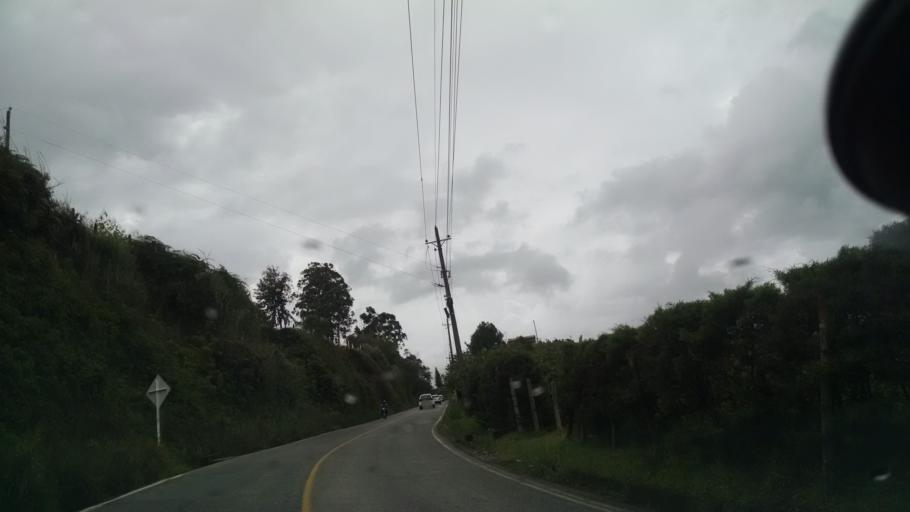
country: CO
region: Antioquia
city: Guatape
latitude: 6.2028
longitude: -75.2084
